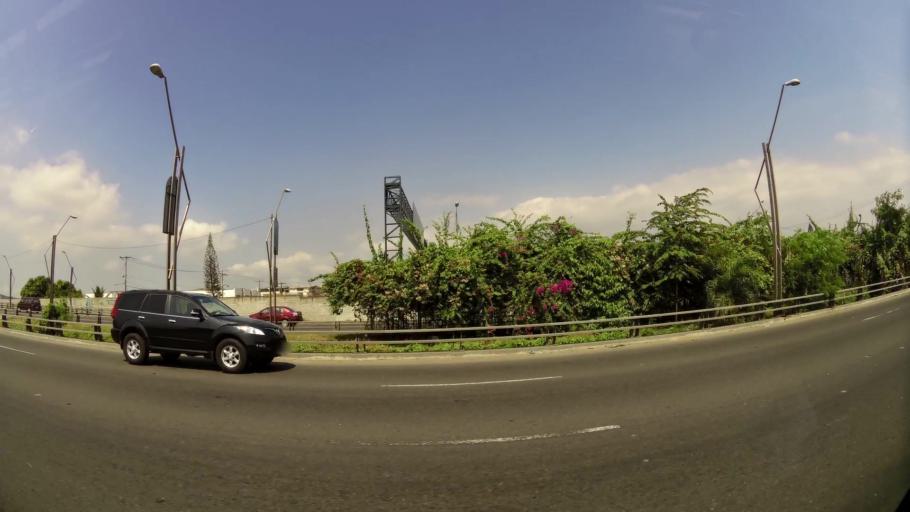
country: EC
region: Guayas
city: Eloy Alfaro
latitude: -2.1535
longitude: -79.8623
